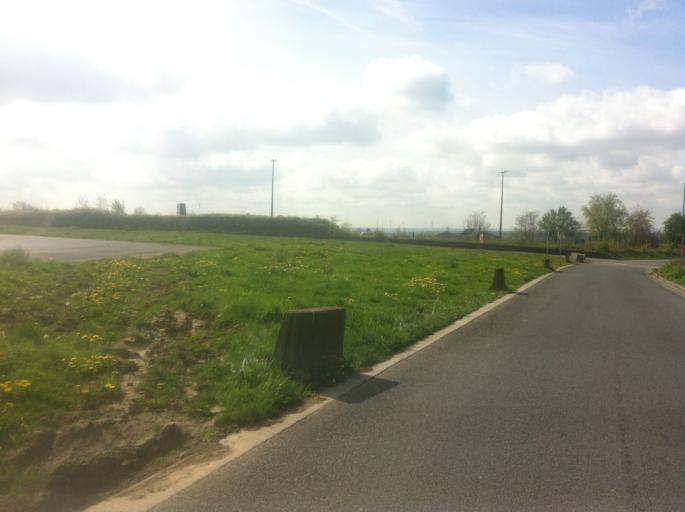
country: BE
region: Wallonia
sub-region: Province du Hainaut
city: Roeulx
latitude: 50.4898
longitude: 4.0926
